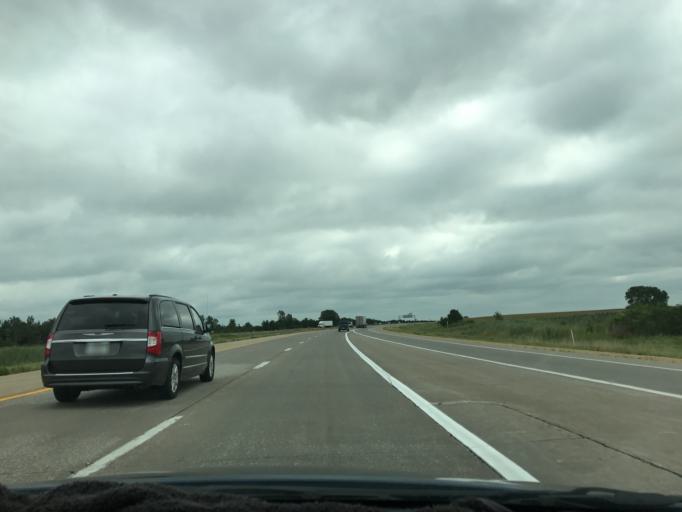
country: US
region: Iowa
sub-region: Scott County
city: Eldridge
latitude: 41.6032
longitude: -90.6707
